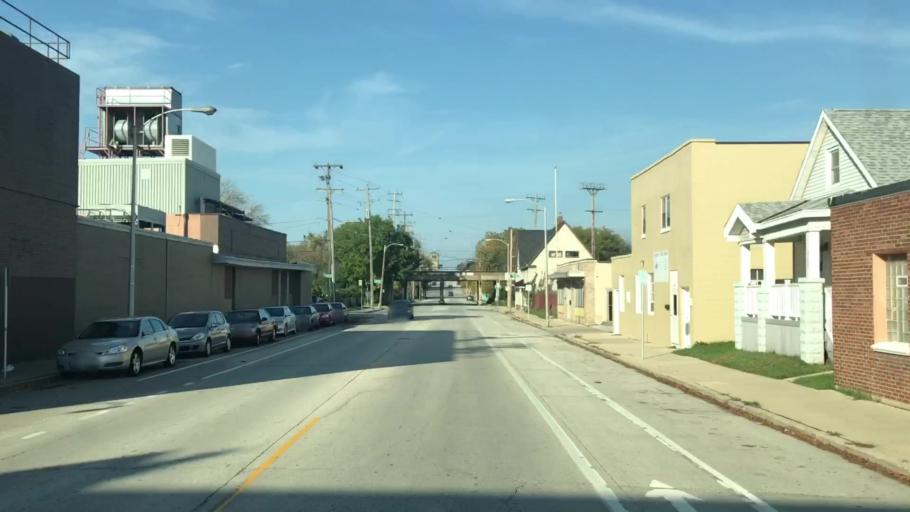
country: US
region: Wisconsin
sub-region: Milwaukee County
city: Milwaukee
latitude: 43.0029
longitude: -87.9070
